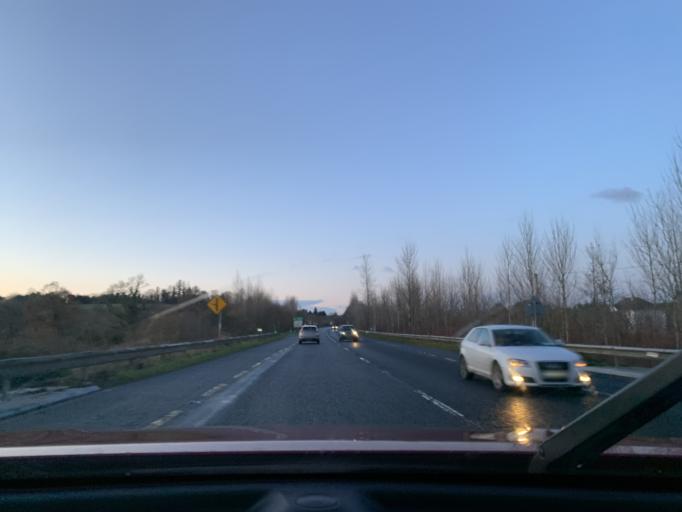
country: IE
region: Connaught
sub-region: County Leitrim
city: Carrick-on-Shannon
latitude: 53.9247
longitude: -7.9953
